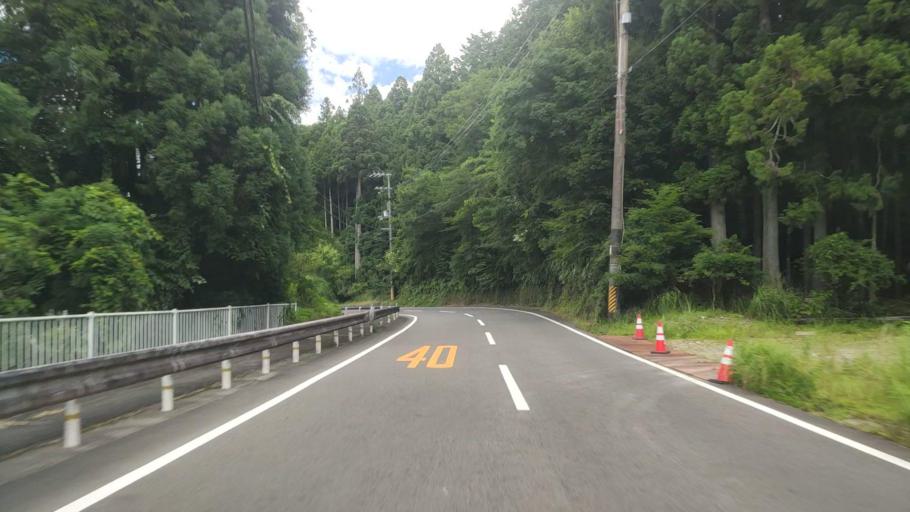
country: JP
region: Mie
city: Owase
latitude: 33.9535
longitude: 136.0688
